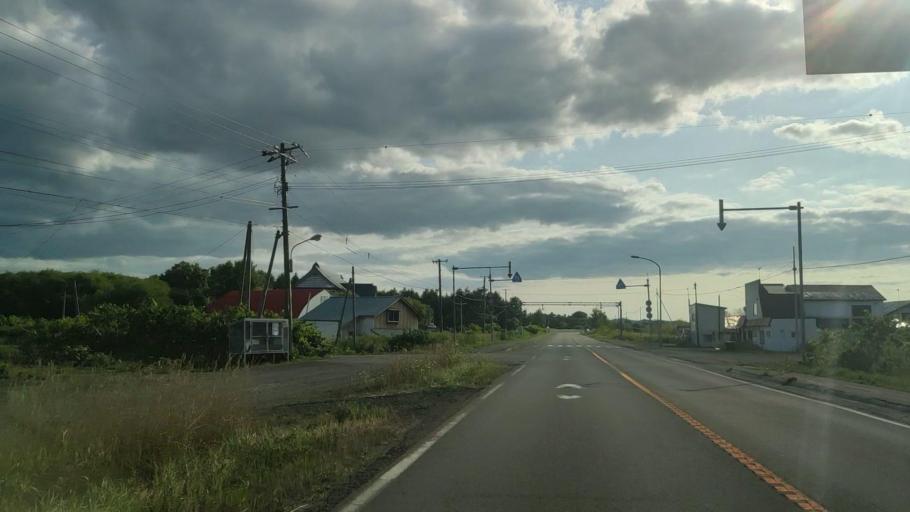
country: JP
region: Hokkaido
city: Makubetsu
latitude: 44.8990
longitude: 141.9319
